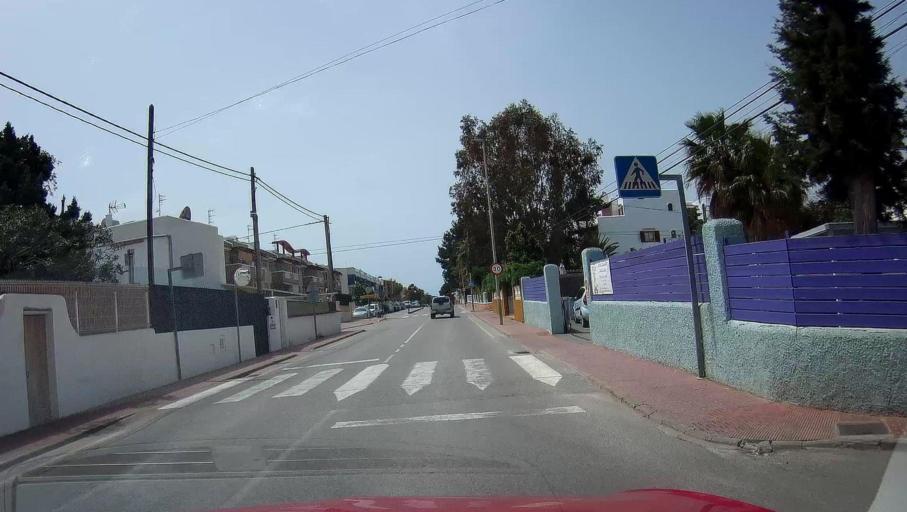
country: ES
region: Balearic Islands
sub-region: Illes Balears
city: Santa Eularia des Riu
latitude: 38.9918
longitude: 1.5470
